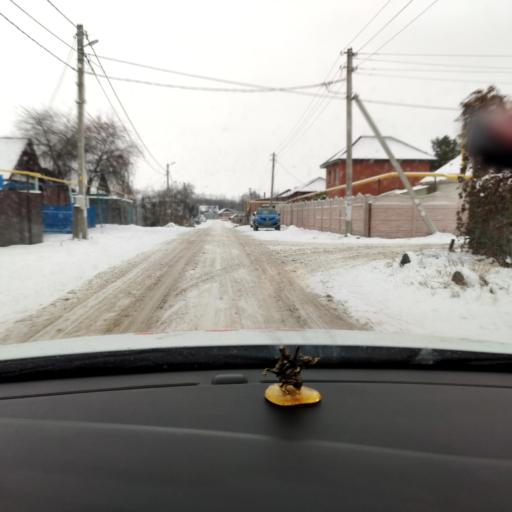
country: RU
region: Tatarstan
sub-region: Gorod Kazan'
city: Kazan
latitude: 55.7385
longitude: 49.0993
